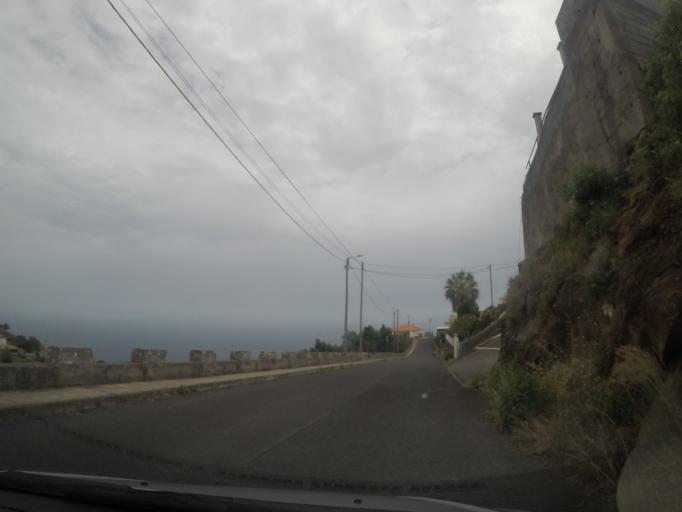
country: PT
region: Madeira
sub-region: Santa Cruz
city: Santa Cruz
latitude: 32.6809
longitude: -16.8093
